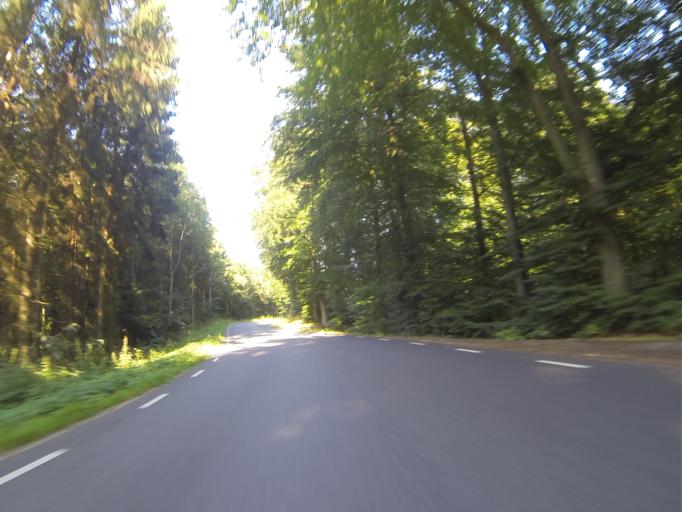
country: SE
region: Skane
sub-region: Lunds Kommun
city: Genarp
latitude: 55.5907
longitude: 13.3589
